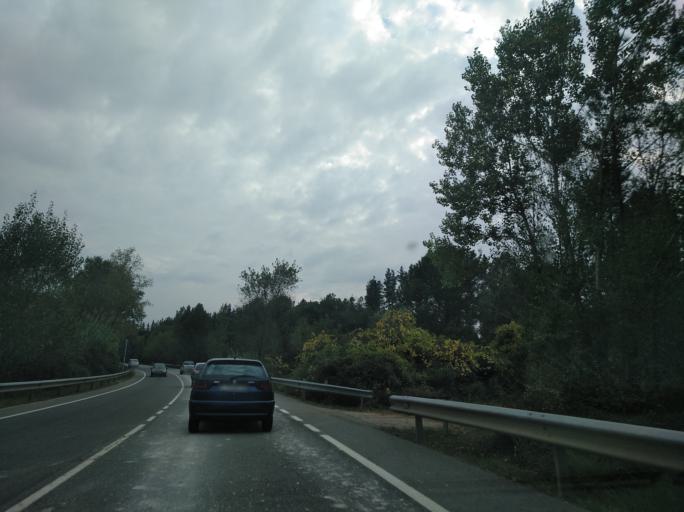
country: ES
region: Catalonia
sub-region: Provincia de Girona
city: Santa Coloma de Farners
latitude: 41.8788
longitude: 2.6579
